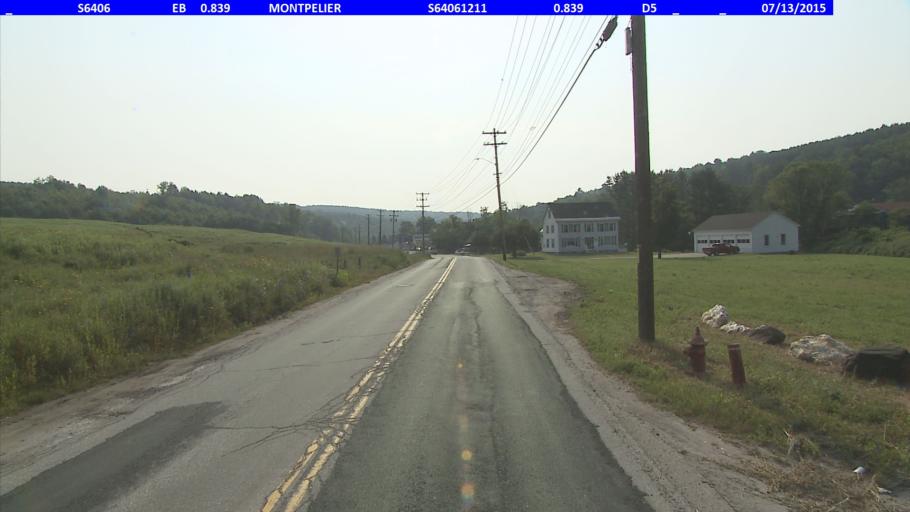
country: US
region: Vermont
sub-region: Washington County
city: Montpelier
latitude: 44.2509
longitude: -72.5648
